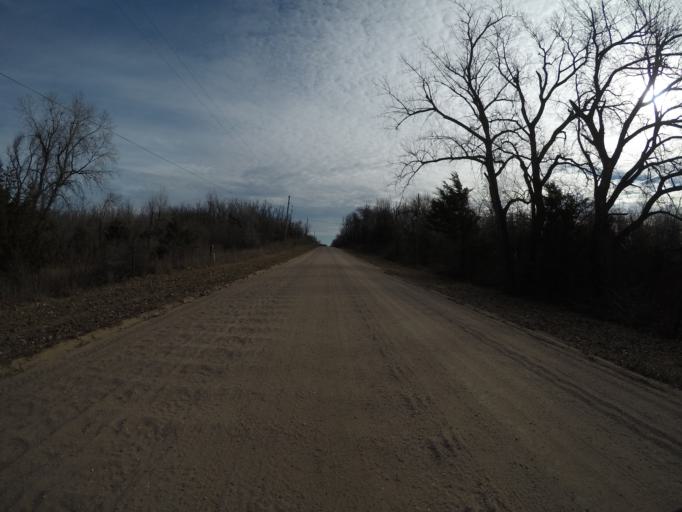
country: US
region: Kansas
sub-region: Reno County
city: Hutchinson
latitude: 38.1011
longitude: -97.8598
